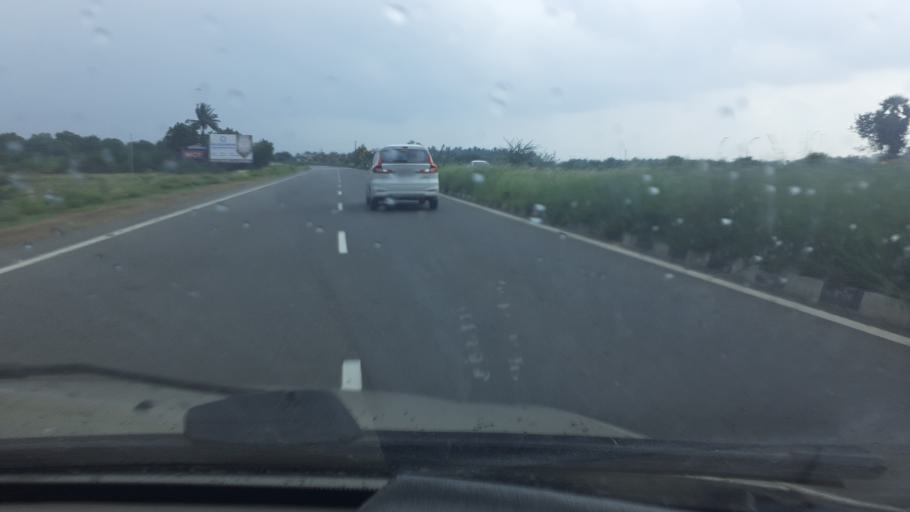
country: IN
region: Tamil Nadu
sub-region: Virudhunagar
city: Virudunagar
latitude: 9.6488
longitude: 77.9644
